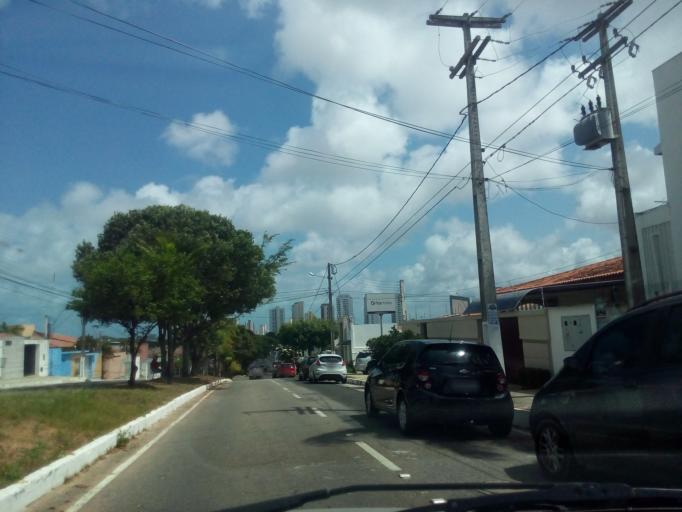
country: BR
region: Rio Grande do Norte
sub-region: Natal
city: Natal
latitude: -5.8496
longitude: -35.2041
